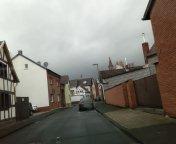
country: DE
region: North Rhine-Westphalia
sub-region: Regierungsbezirk Koln
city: Bonn
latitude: 50.7728
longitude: 7.0924
